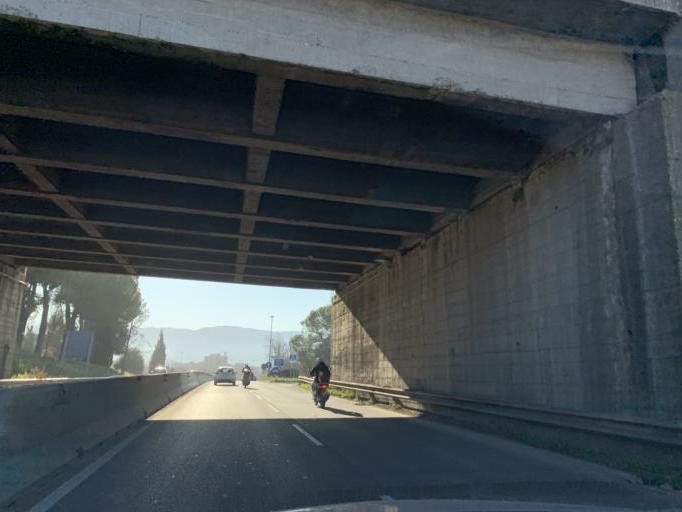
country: IT
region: Umbria
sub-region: Provincia di Terni
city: Terni
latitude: 42.5739
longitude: 12.6276
